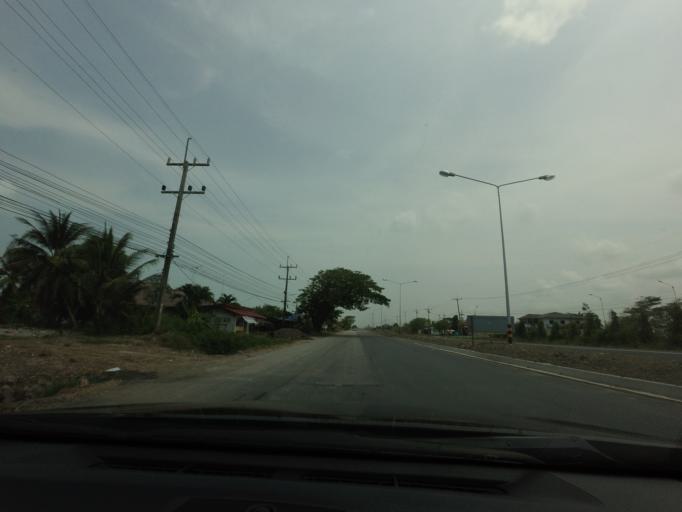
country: TH
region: Songkhla
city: Ranot
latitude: 7.8863
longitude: 100.3437
